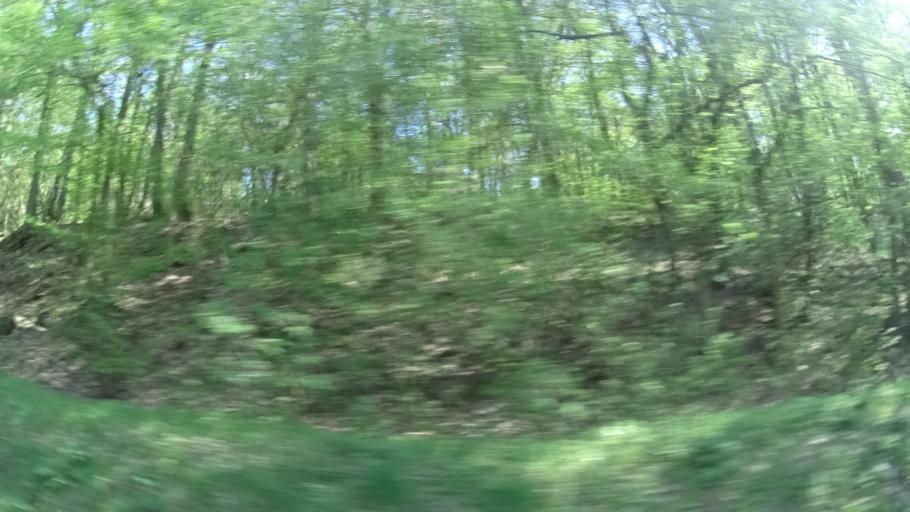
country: DE
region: Bavaria
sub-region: Regierungsbezirk Unterfranken
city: Hofheim in Unterfranken
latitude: 50.1336
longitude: 10.5774
